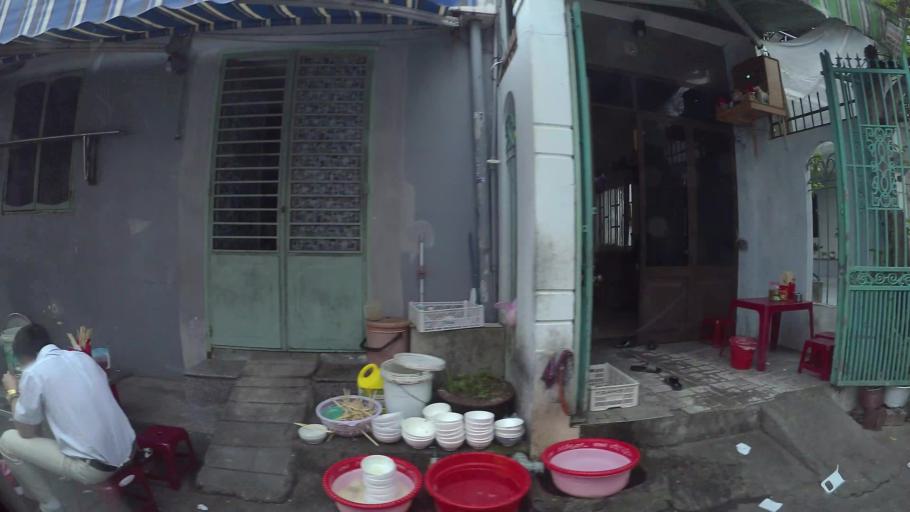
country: VN
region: Da Nang
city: Thanh Khe
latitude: 16.0707
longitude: 108.1987
